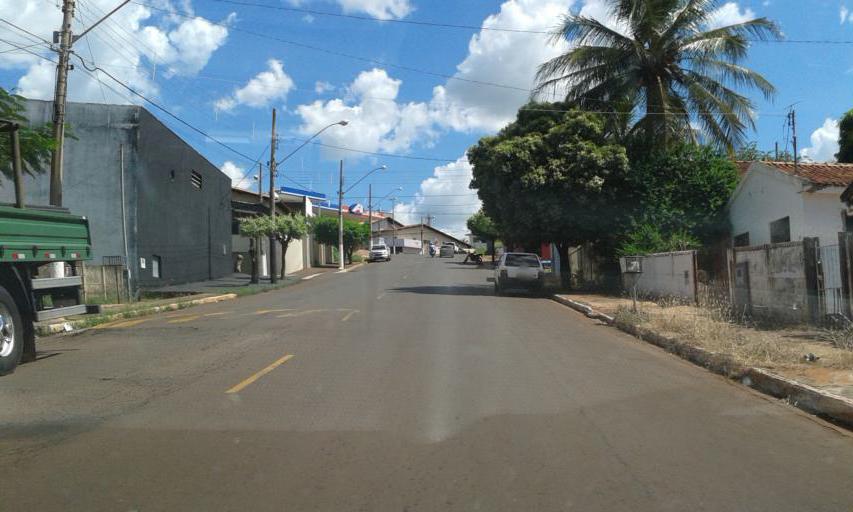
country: BR
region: Minas Gerais
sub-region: Ituiutaba
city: Ituiutaba
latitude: -18.9638
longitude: -49.4632
